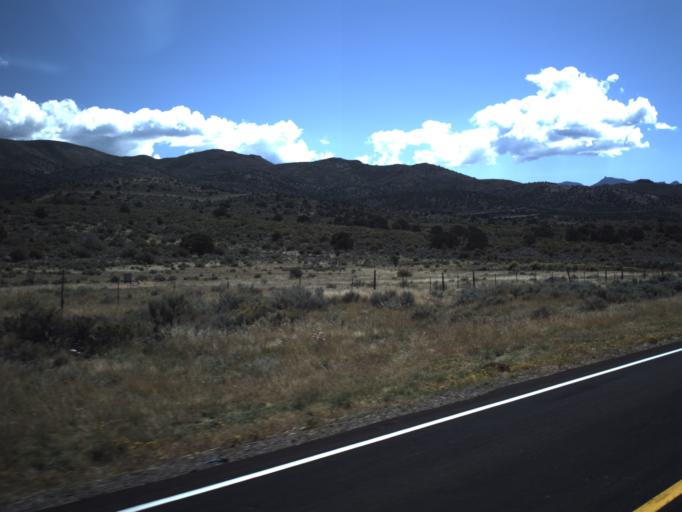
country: US
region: Utah
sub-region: Washington County
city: Enterprise
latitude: 37.4990
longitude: -113.6315
